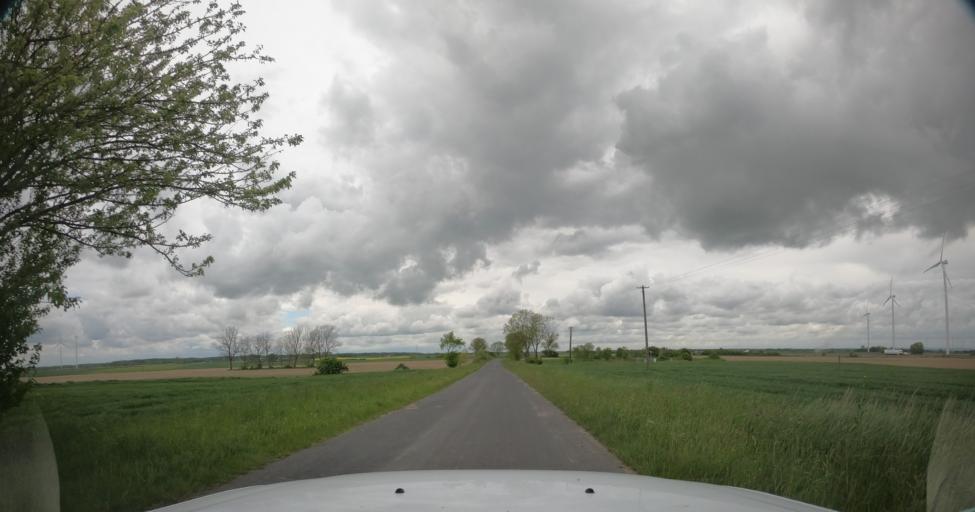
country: PL
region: West Pomeranian Voivodeship
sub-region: Powiat pyrzycki
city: Kozielice
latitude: 53.0958
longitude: 14.8023
